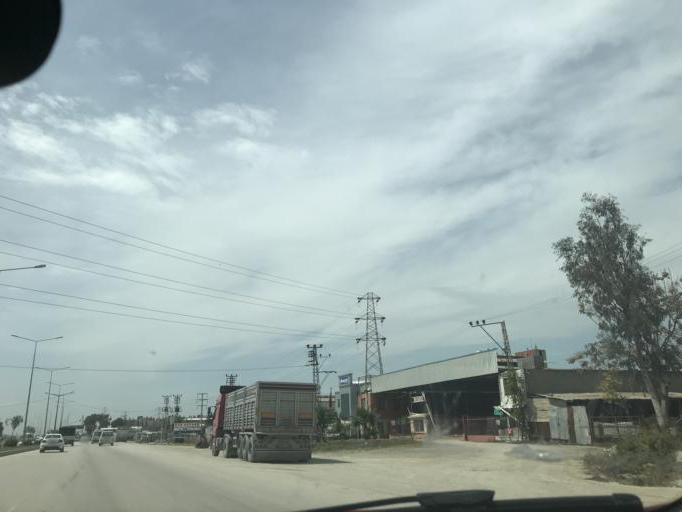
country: TR
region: Adana
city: Yuregir
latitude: 36.9819
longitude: 35.4362
